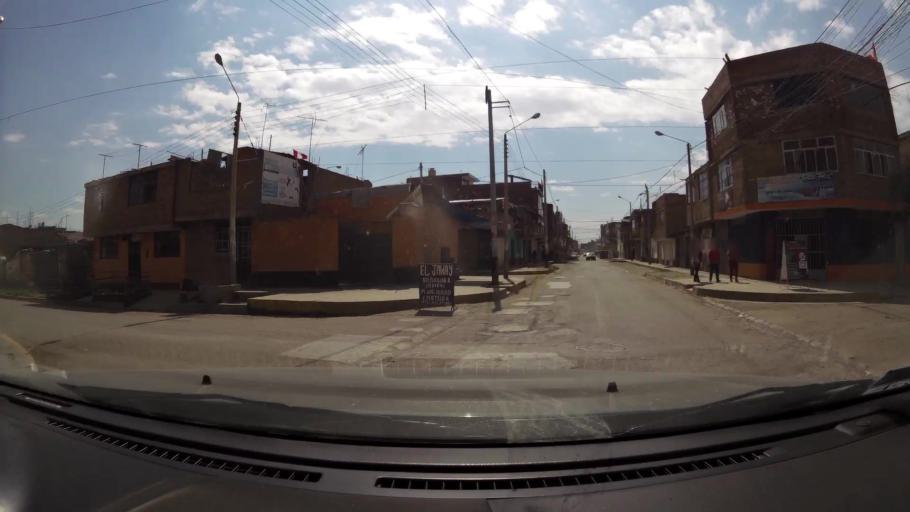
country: PE
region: Junin
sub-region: Provincia de Huancayo
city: Huancayo
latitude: -12.0878
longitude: -75.2042
